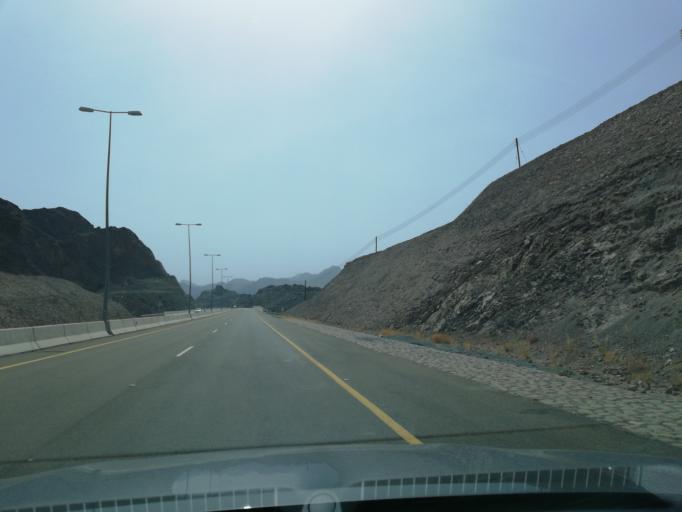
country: OM
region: Al Batinah
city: Al Liwa'
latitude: 24.2615
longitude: 56.3712
